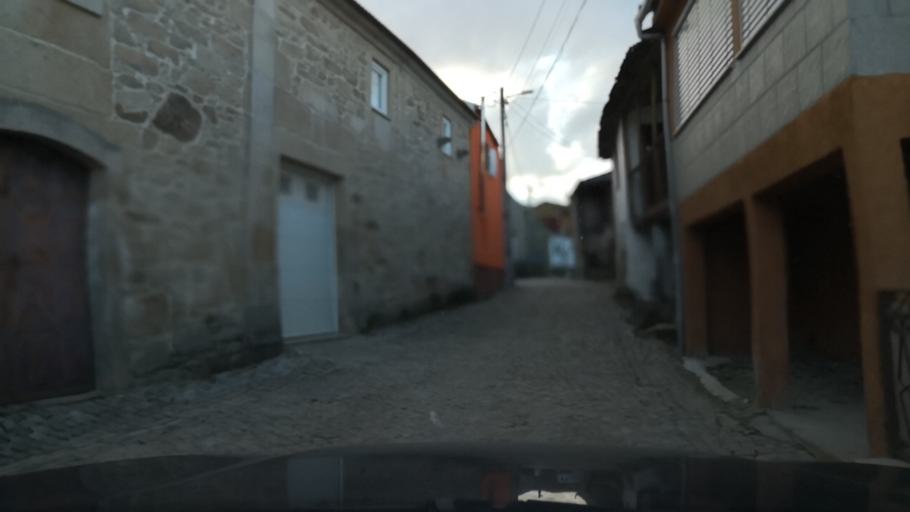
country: PT
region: Braganca
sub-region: Carrazeda de Ansiaes
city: Carrazeda de Anciaes
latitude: 41.2203
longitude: -7.3485
